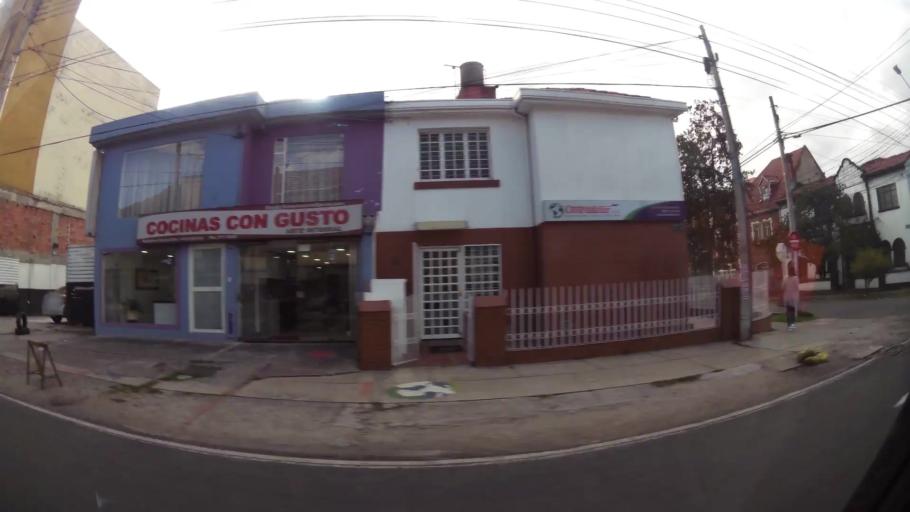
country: CO
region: Bogota D.C.
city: Bogota
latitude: 4.6452
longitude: -74.0686
